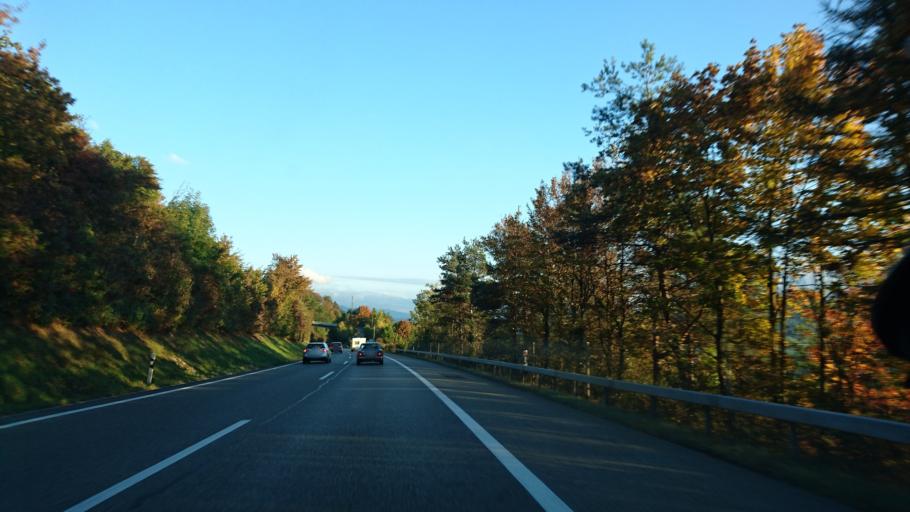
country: CH
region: Bern
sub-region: Bern-Mittelland District
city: Belp
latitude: 46.9124
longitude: 7.5147
